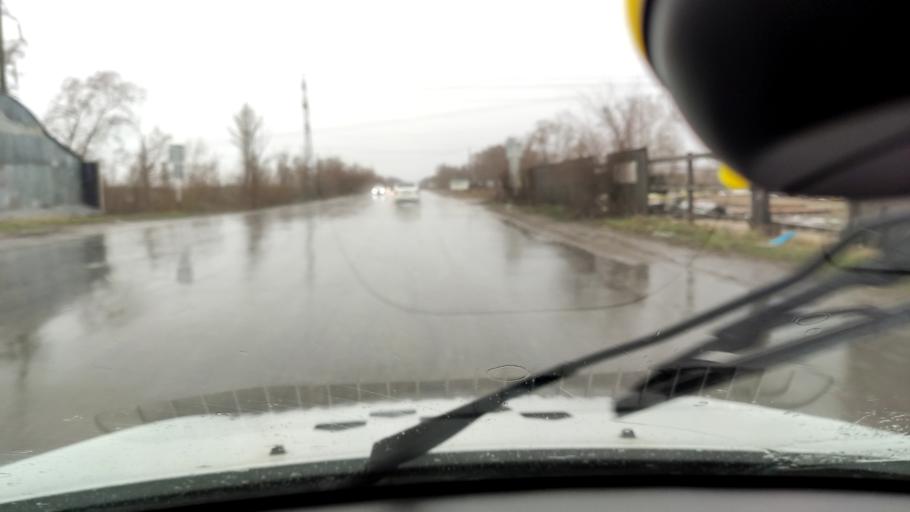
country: RU
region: Samara
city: Tol'yatti
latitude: 53.5799
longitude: 49.4033
